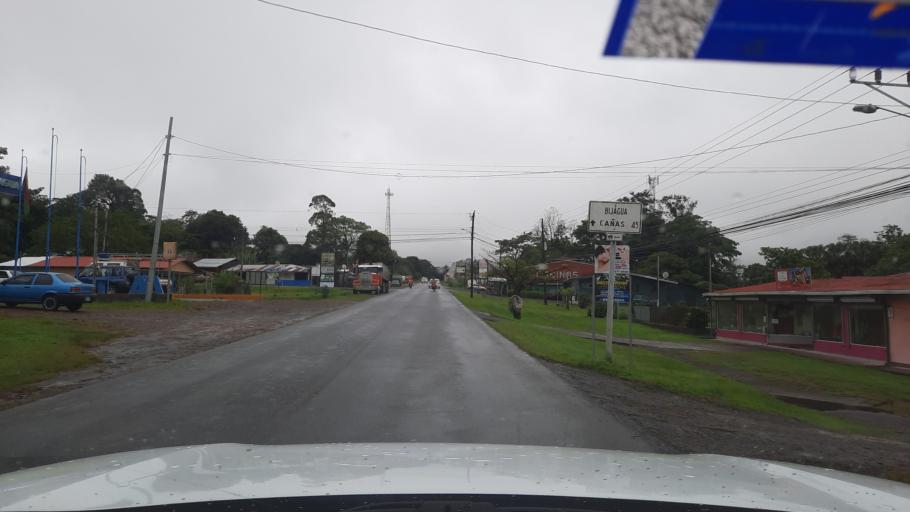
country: CR
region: Alajuela
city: Bijagua
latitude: 10.7312
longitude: -85.0557
